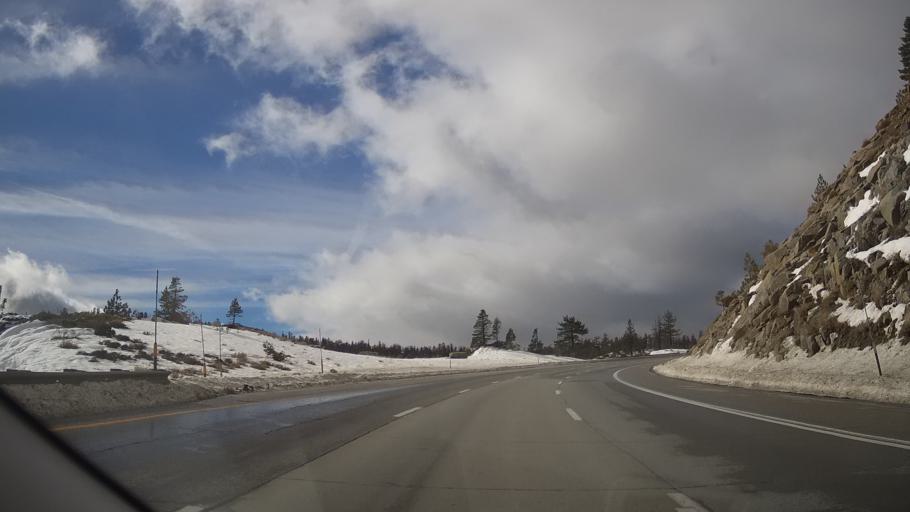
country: US
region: California
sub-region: Nevada County
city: Truckee
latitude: 39.3417
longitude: -120.3190
